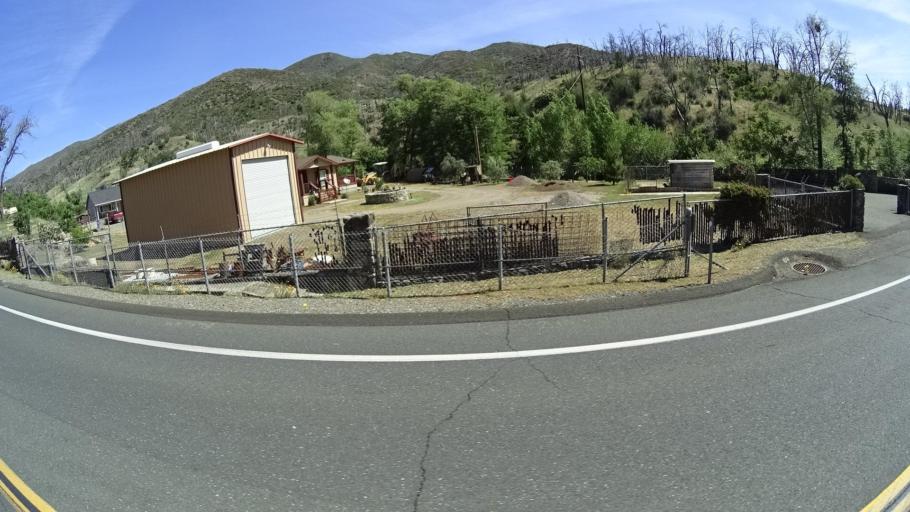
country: US
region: California
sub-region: Lake County
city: Cobb
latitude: 38.7787
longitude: -122.6816
